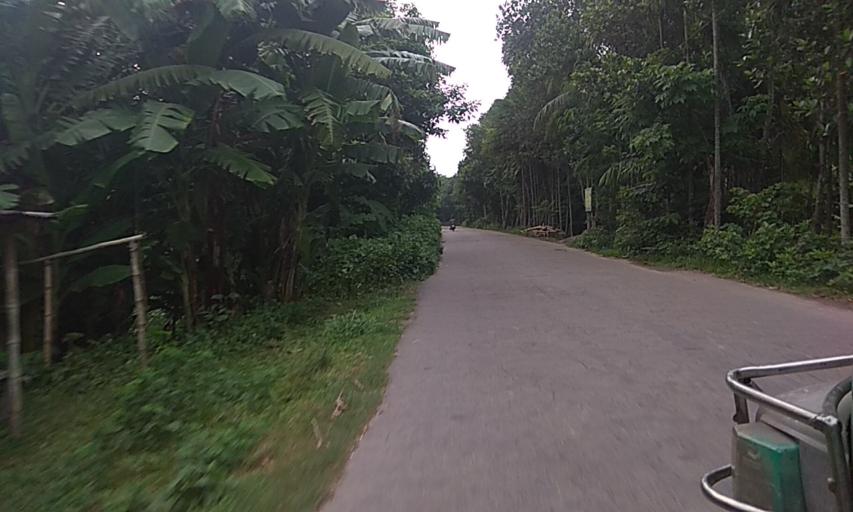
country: BD
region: Dhaka
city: Dohar
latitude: 23.4599
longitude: 89.9984
